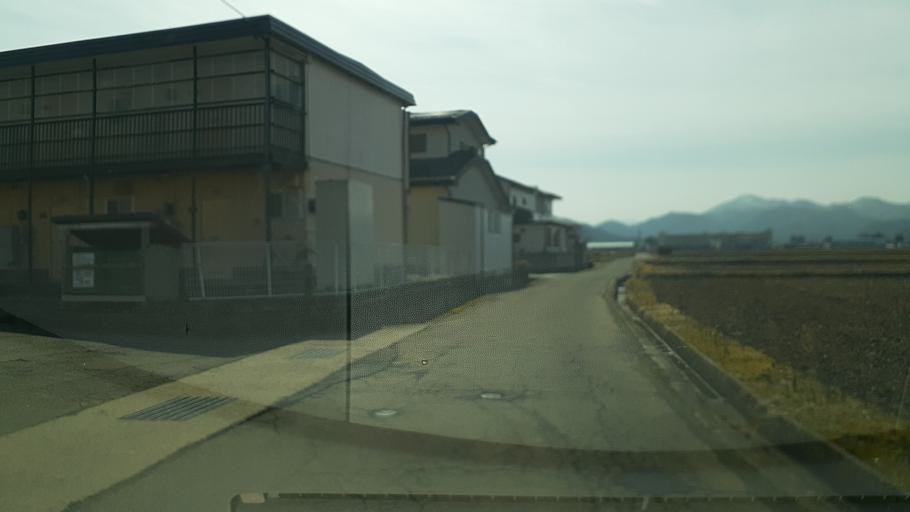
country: JP
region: Fukushima
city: Kitakata
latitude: 37.4675
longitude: 139.9207
